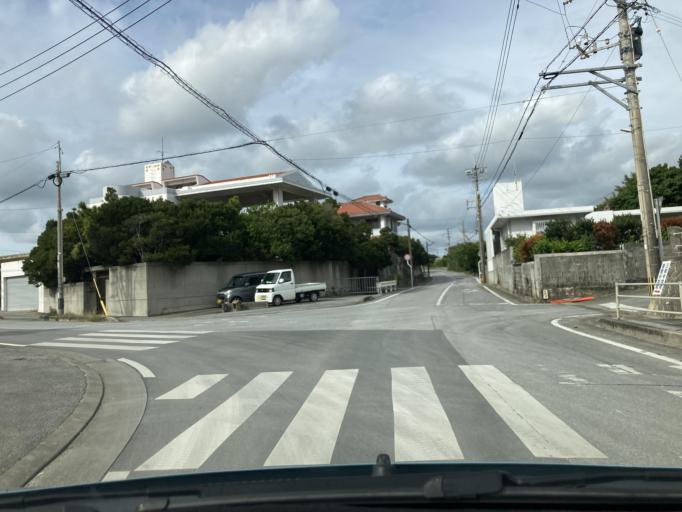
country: JP
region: Okinawa
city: Itoman
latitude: 26.1060
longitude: 127.6886
